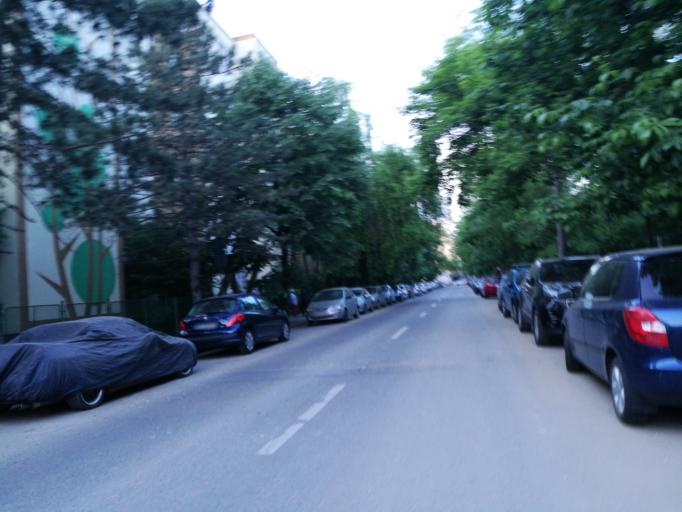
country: RO
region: Ilfov
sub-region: Comuna Chiajna
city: Rosu
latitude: 44.4660
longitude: 26.0600
